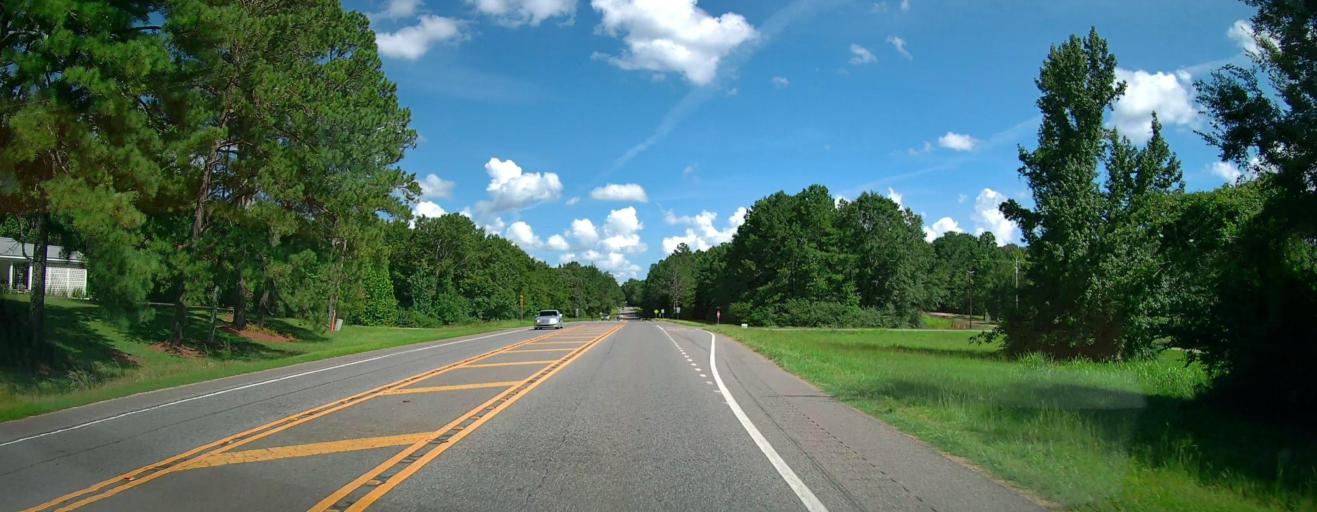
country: US
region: Alabama
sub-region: Pickens County
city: Gordo
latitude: 33.2971
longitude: -87.8772
